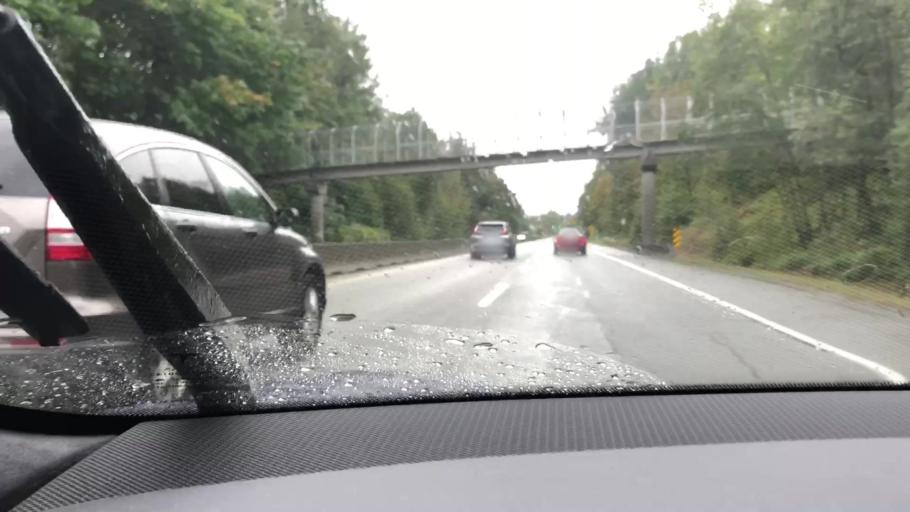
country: CA
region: British Columbia
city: Burnaby
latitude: 49.2626
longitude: -122.9037
